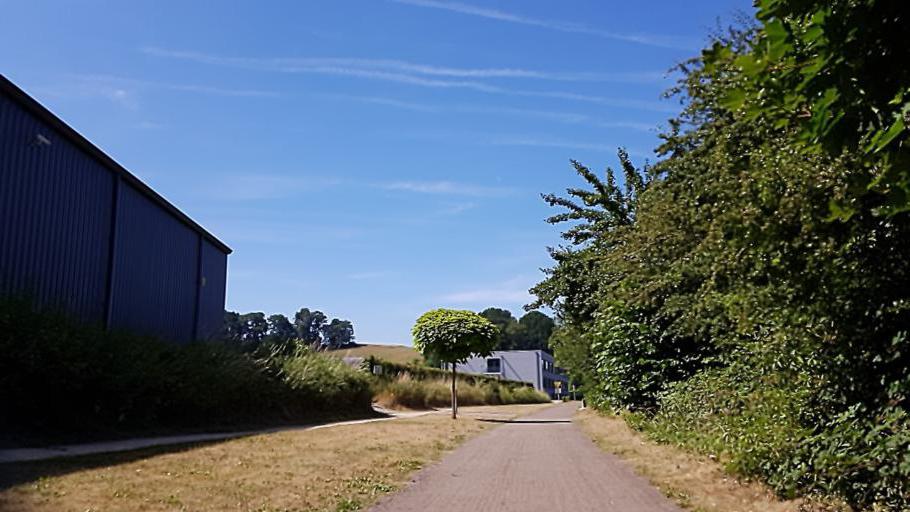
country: BE
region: Wallonia
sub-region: Province du Brabant Wallon
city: Court-Saint-Etienne
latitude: 50.6457
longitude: 4.5646
